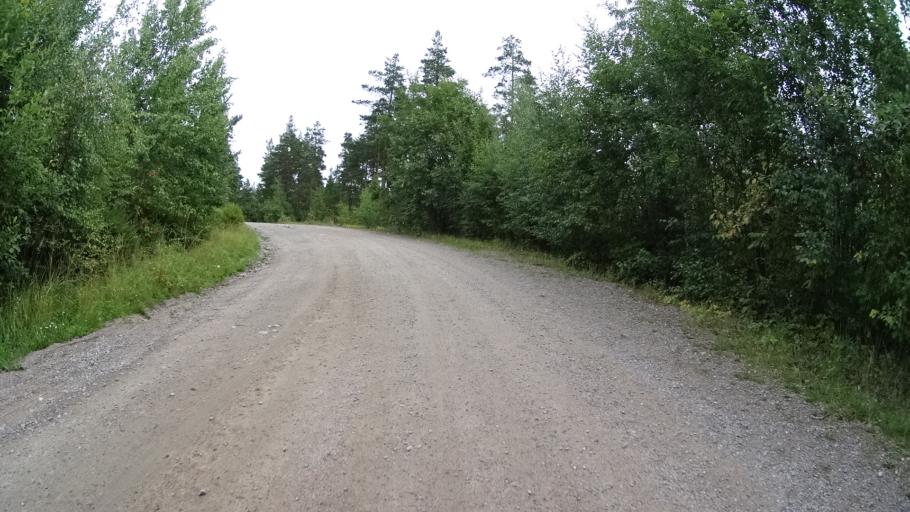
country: FI
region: Uusimaa
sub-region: Helsinki
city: Teekkarikylae
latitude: 60.2837
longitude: 24.8940
